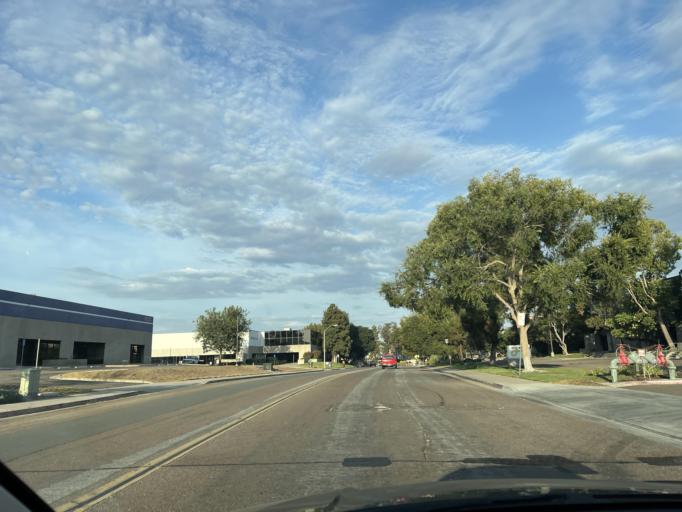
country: US
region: California
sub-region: San Diego County
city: Fairbanks Ranch
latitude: 32.8961
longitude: -117.1400
